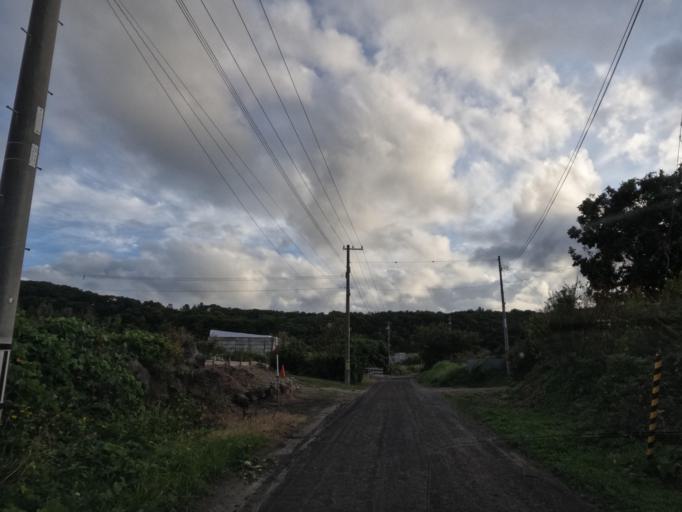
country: JP
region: Hokkaido
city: Date
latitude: 42.3813
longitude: 140.9129
